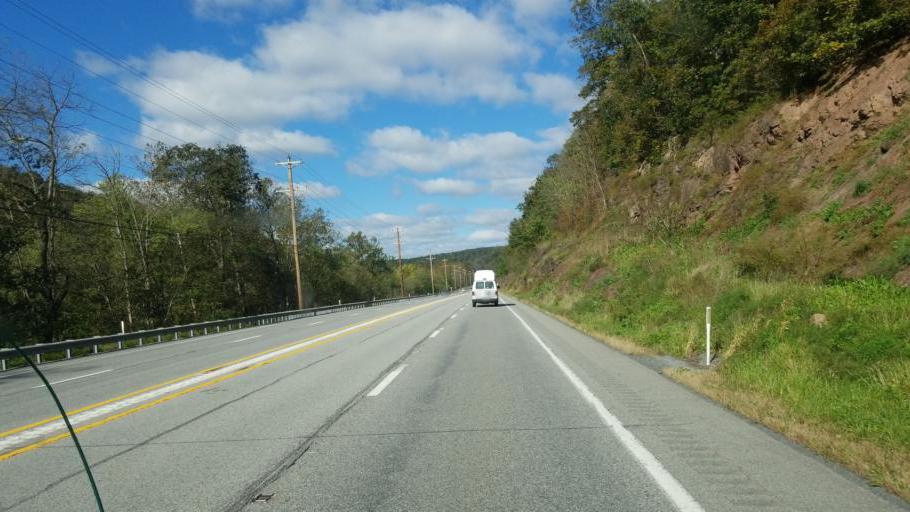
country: US
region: Pennsylvania
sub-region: Bedford County
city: Earlston
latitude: 40.0001
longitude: -78.2936
